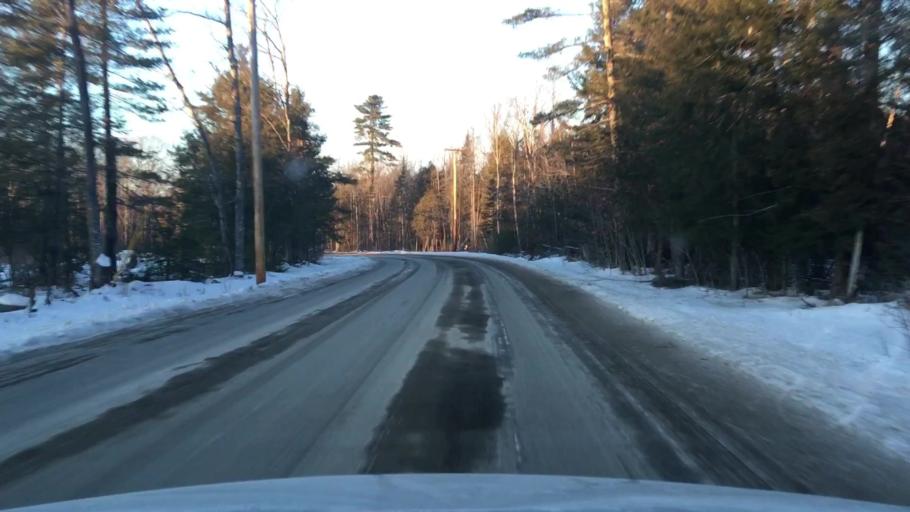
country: US
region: Maine
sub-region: Penobscot County
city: Orrington
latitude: 44.7121
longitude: -68.7529
